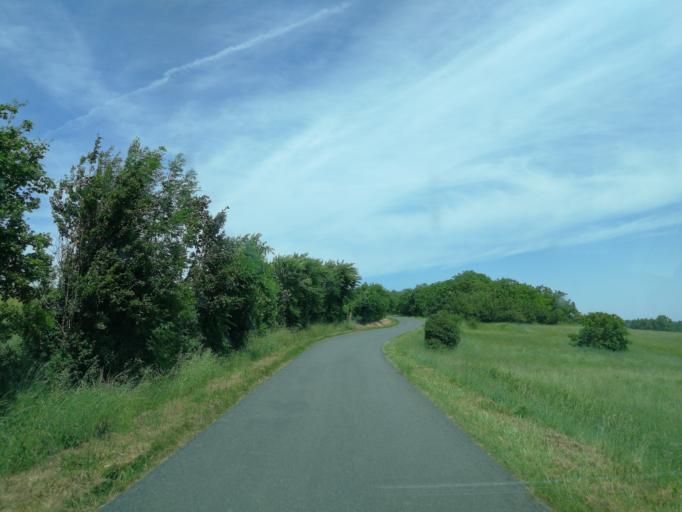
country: FR
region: Pays de la Loire
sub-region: Departement de la Vendee
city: Le Langon
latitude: 46.4270
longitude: -0.8924
